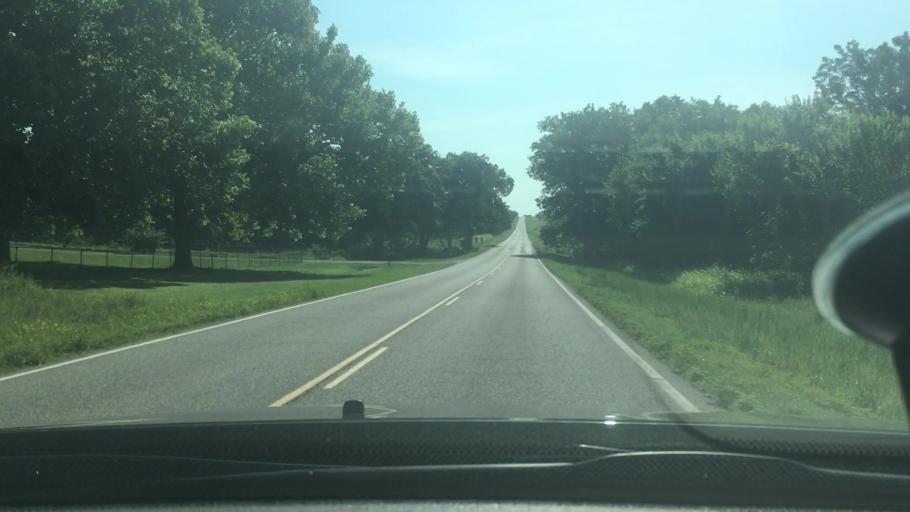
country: US
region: Oklahoma
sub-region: Garvin County
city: Pauls Valley
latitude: 34.6519
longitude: -97.2961
